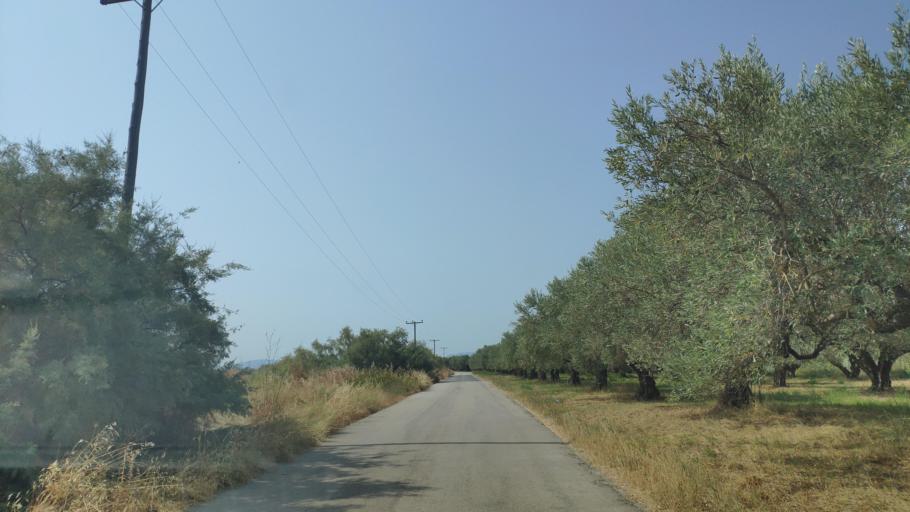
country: GR
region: West Greece
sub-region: Nomos Aitolias kai Akarnanias
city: Menidi
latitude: 39.0465
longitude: 21.0722
